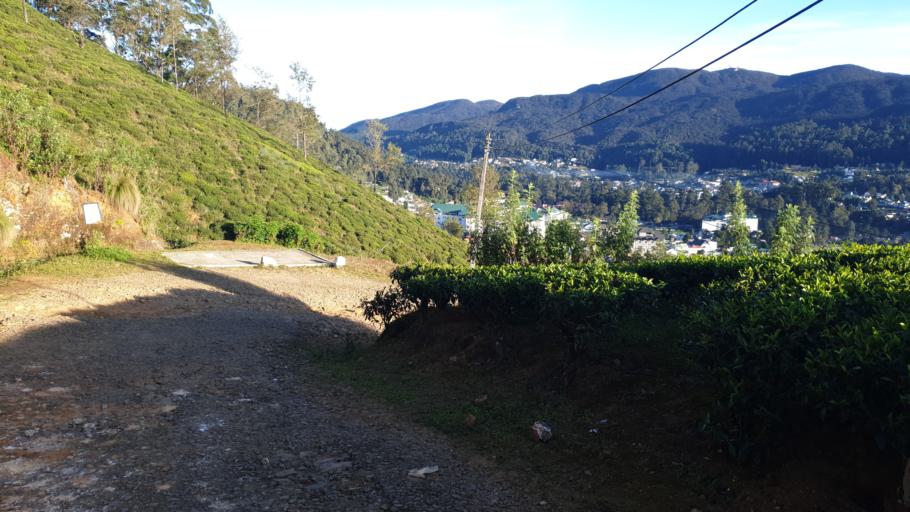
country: LK
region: Central
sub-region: Nuwara Eliya District
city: Nuwara Eliya
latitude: 6.9568
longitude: 80.7647
